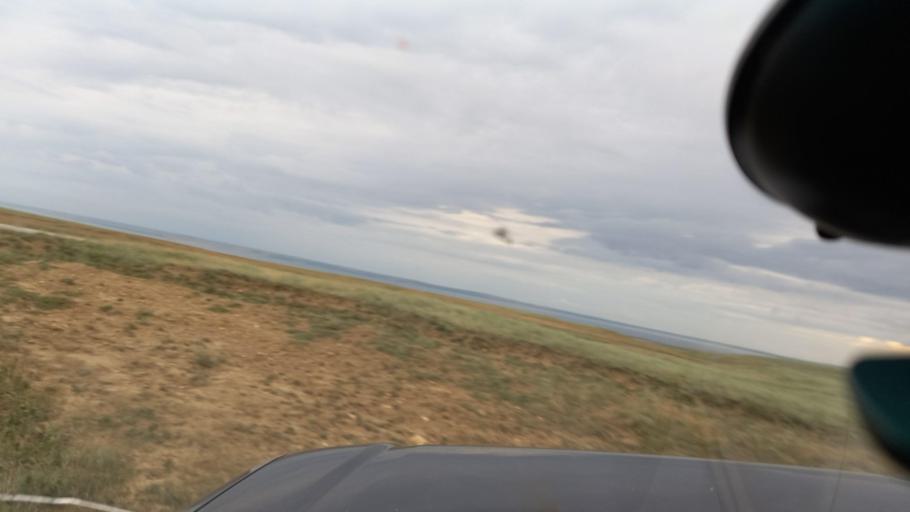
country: RU
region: Krasnodarskiy
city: Taman'
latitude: 45.2050
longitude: 36.7894
